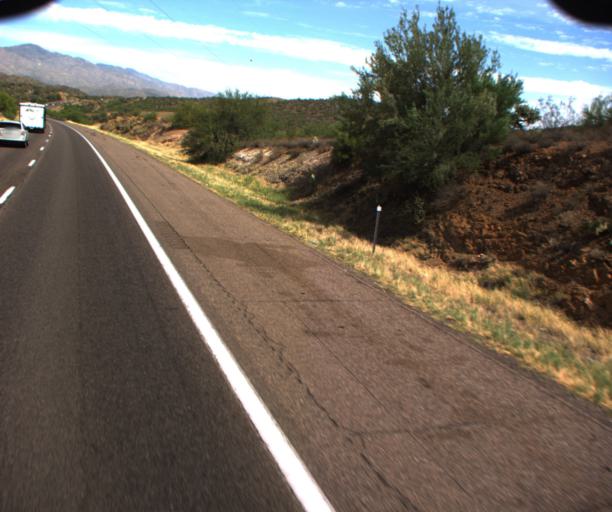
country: US
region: Arizona
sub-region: Yavapai County
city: Black Canyon City
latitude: 34.0156
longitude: -112.1385
